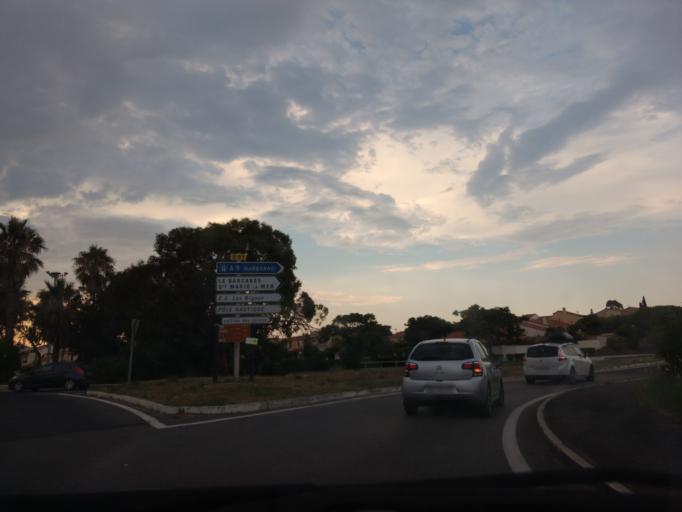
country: FR
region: Languedoc-Roussillon
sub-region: Departement des Pyrenees-Orientales
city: Canet-en-Roussillon
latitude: 42.7031
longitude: 3.0161
